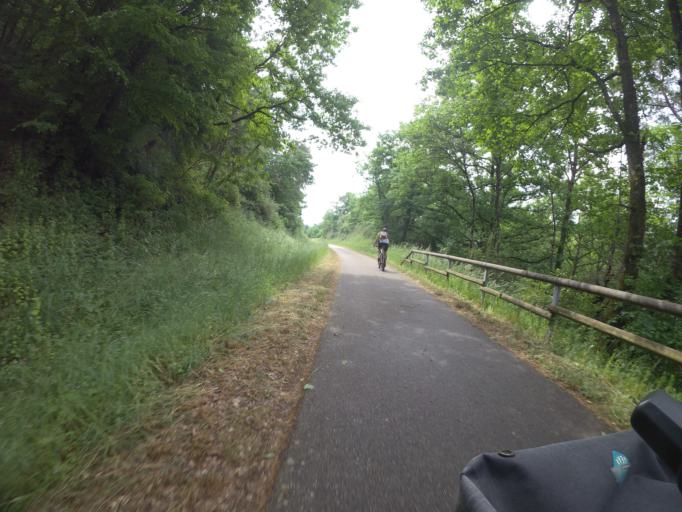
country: DE
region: Rheinland-Pfalz
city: Wittlich
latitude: 50.0019
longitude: 6.8828
